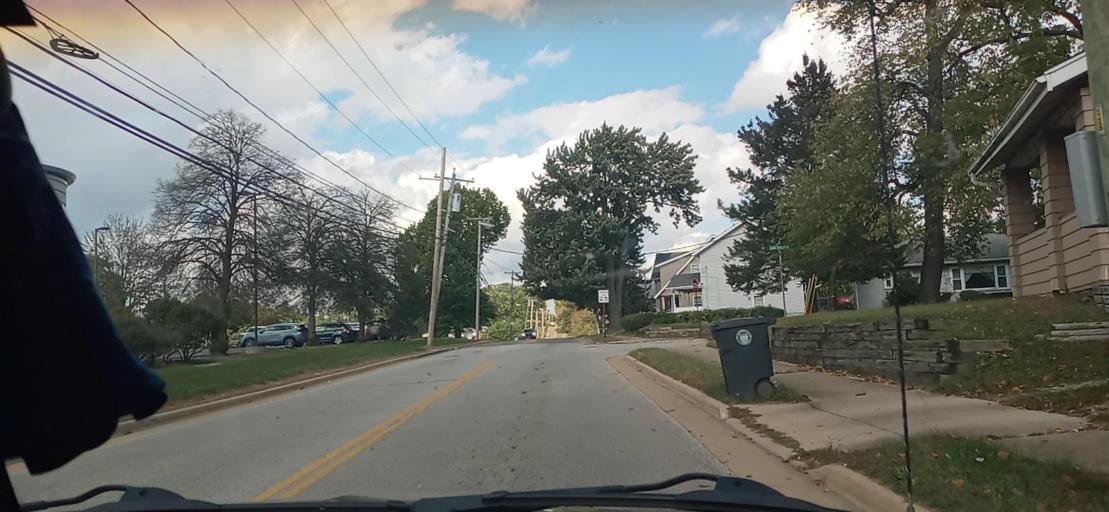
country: US
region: Ohio
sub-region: Summit County
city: Akron
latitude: 41.0916
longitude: -81.4960
